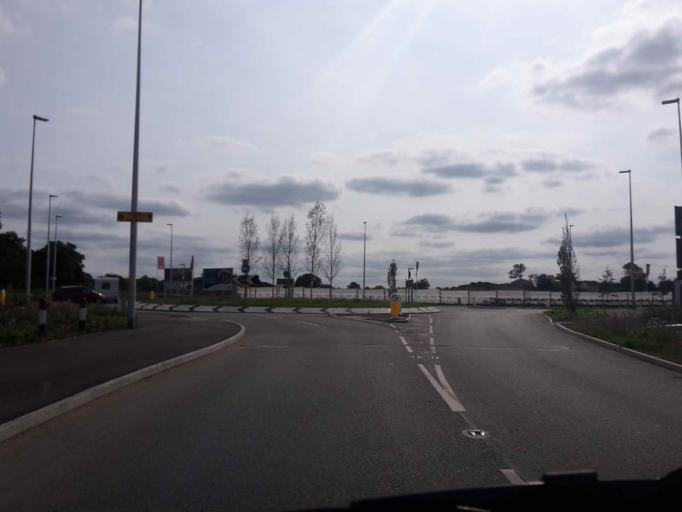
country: GB
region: England
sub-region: Wokingham
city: Wokingham
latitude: 51.4241
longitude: -0.8402
